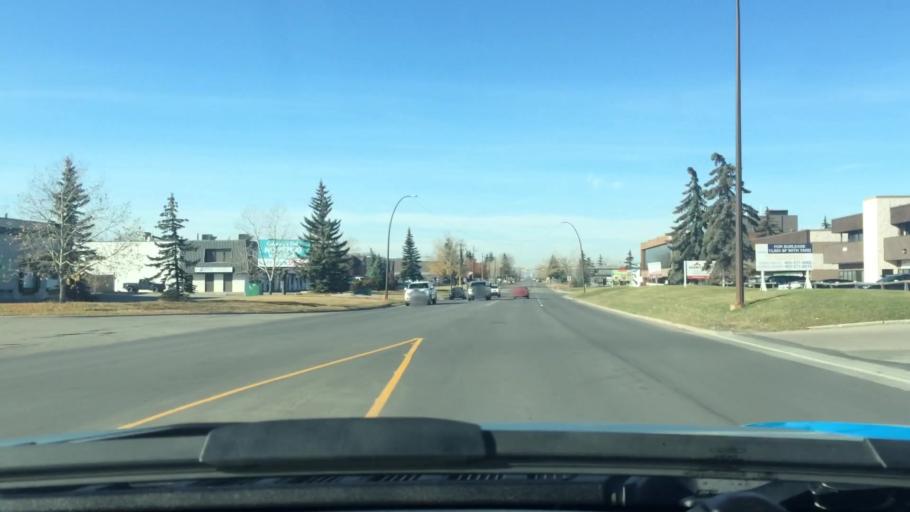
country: CA
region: Alberta
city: Calgary
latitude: 51.0769
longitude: -114.0068
